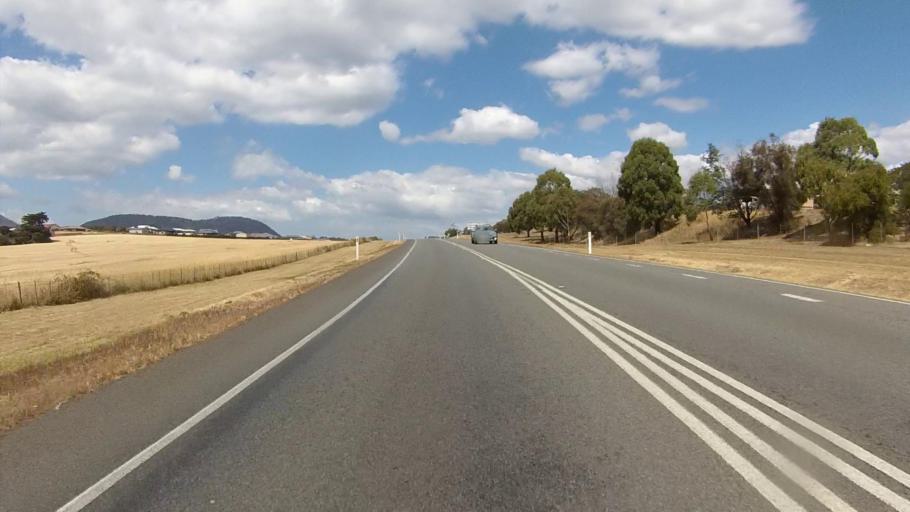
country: AU
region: Tasmania
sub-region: Brighton
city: Old Beach
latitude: -42.7591
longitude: 147.2678
